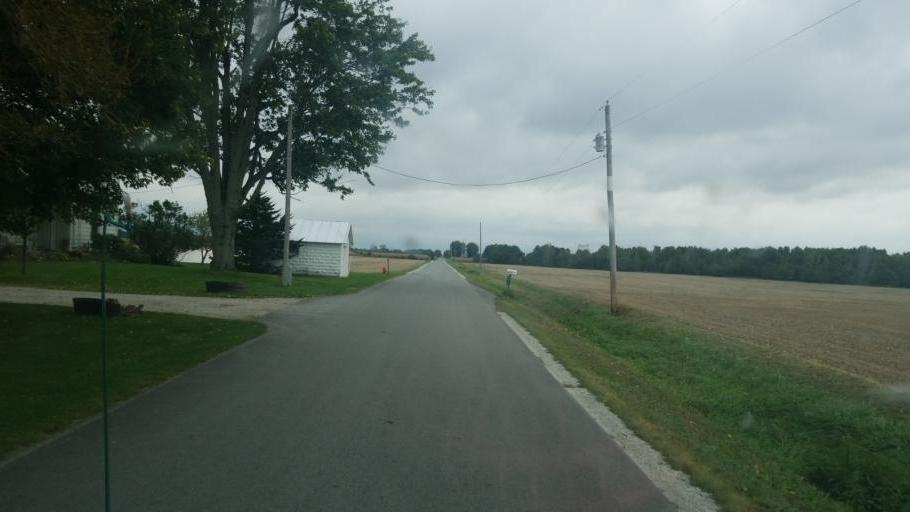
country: US
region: Ohio
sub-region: Seneca County
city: Fostoria
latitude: 41.0862
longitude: -83.5166
